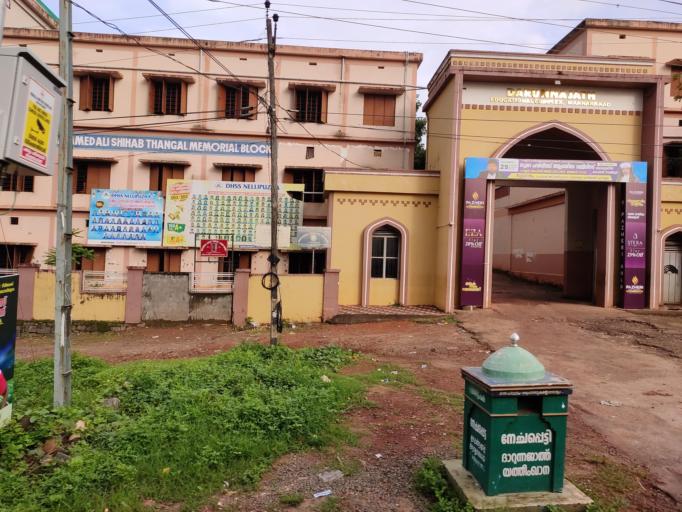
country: IN
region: Kerala
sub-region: Palakkad district
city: Mannarakkat
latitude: 10.9986
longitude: 76.4701
